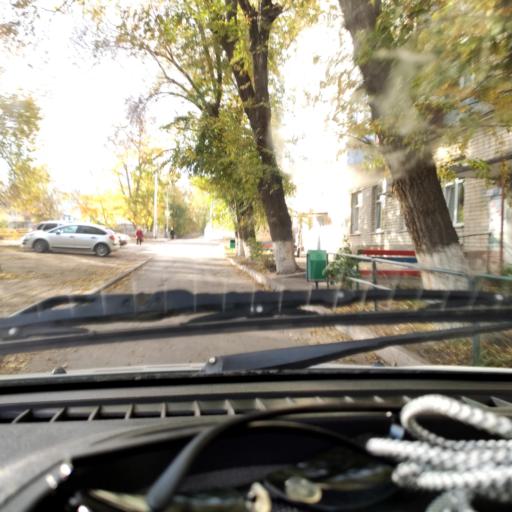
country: RU
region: Samara
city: Zhigulevsk
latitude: 53.4852
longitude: 49.4809
